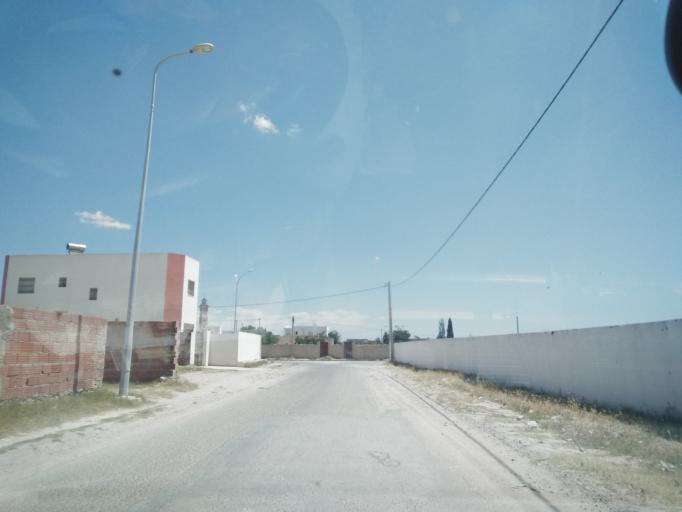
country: TN
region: Safaqis
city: Al Qarmadah
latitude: 34.8240
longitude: 10.7703
